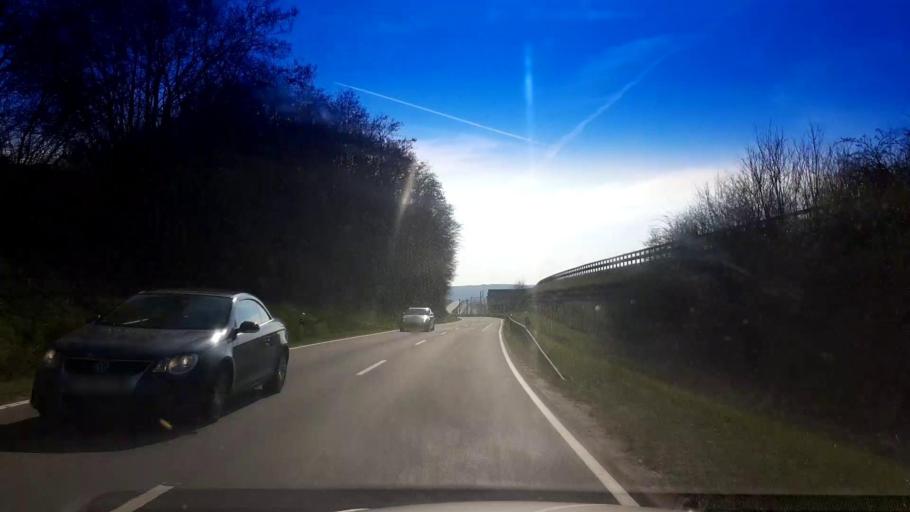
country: DE
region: Bavaria
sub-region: Upper Franconia
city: Breitengussbach
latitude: 49.9905
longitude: 10.9066
